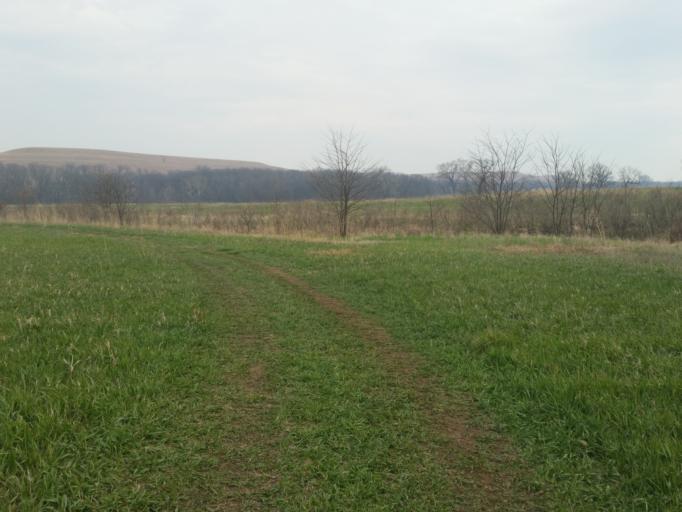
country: US
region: Kansas
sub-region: Chase County
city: Cottonwood Falls
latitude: 38.4286
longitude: -96.5541
